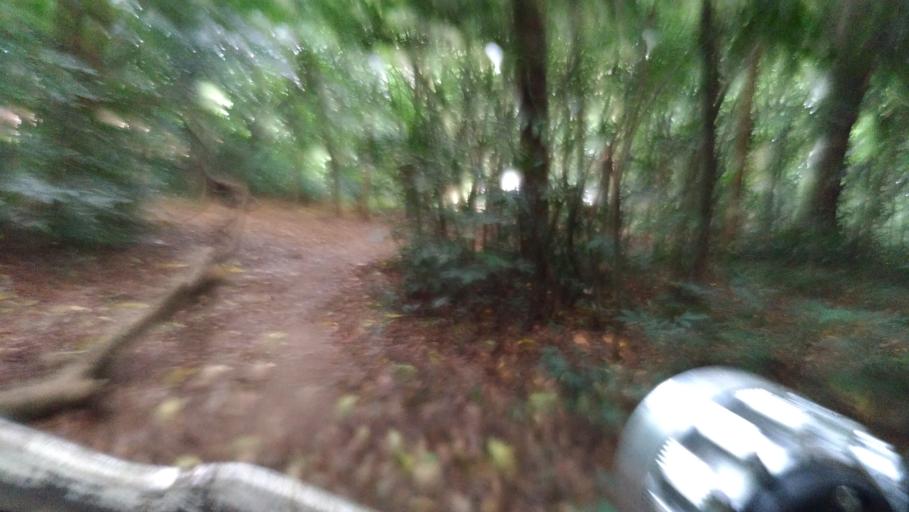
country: ID
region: West Java
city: Cileungsir
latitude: -6.3688
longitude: 106.9016
